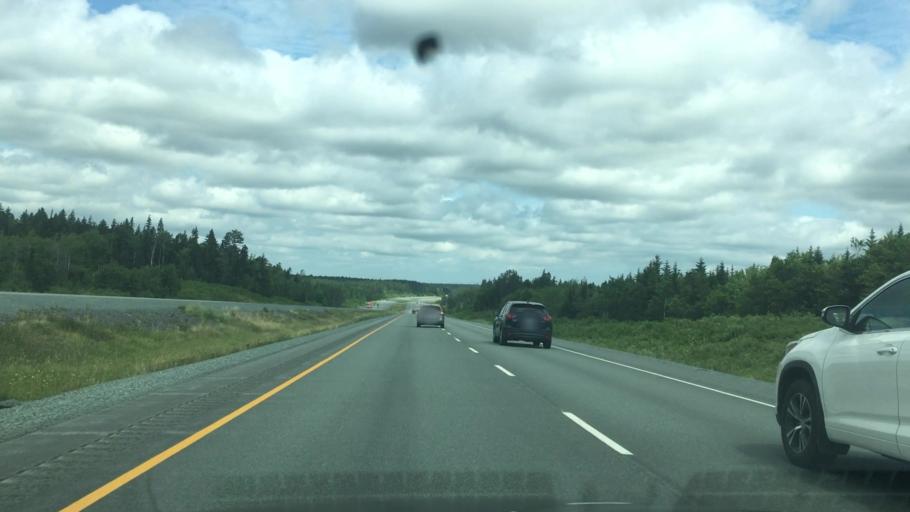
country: CA
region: Nova Scotia
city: Oxford
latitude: 45.6354
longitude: -63.7445
